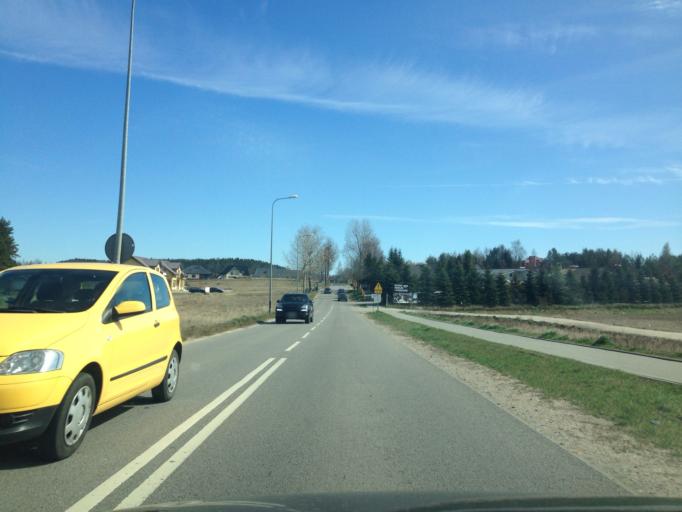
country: PL
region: Pomeranian Voivodeship
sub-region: Powiat kartuski
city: Chwaszczyno
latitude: 54.4870
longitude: 18.4303
